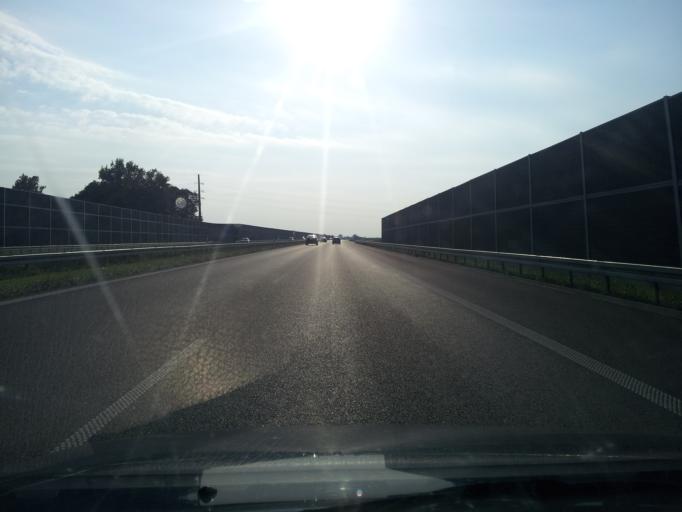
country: PL
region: Masovian Voivodeship
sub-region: Powiat zyrardowski
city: Wiskitki
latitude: 52.1014
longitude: 20.4249
